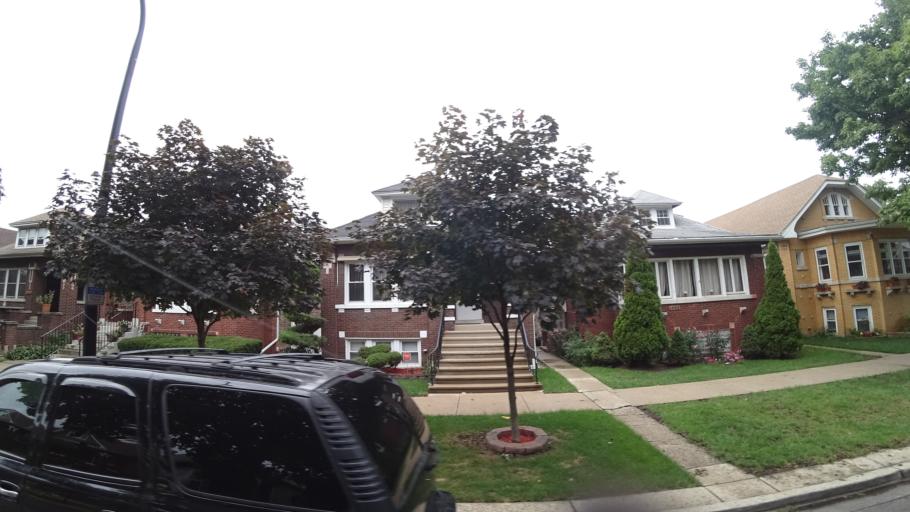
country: US
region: Illinois
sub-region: Cook County
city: Cicero
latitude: 41.8597
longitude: -87.7703
